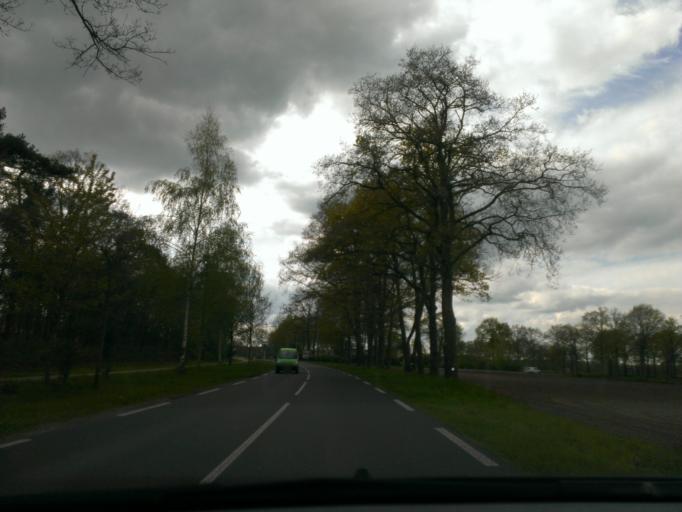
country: NL
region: Overijssel
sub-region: Gemeente Borne
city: Borne
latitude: 52.3142
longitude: 6.6968
